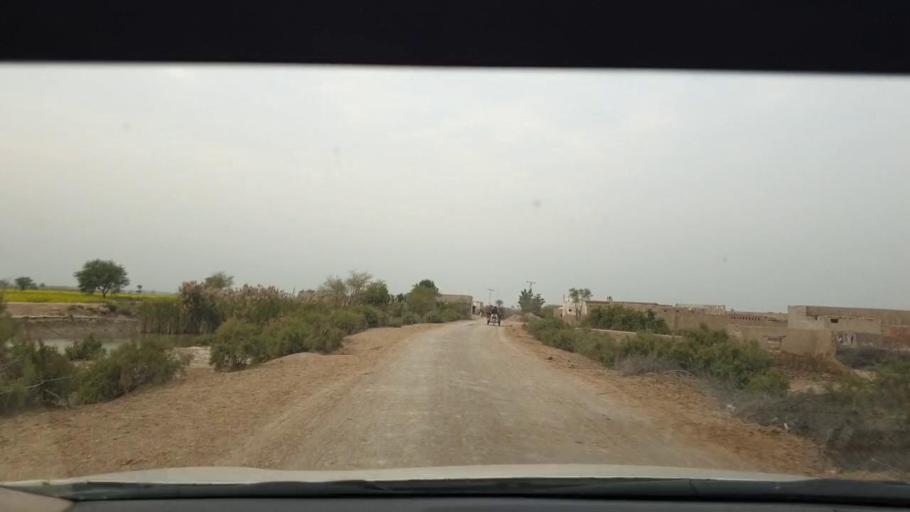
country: PK
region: Sindh
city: Sinjhoro
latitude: 25.9210
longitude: 68.7558
